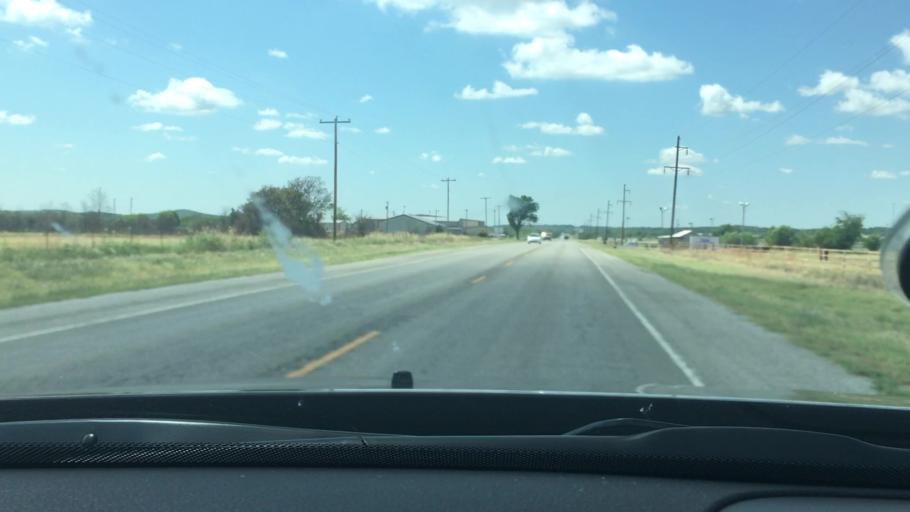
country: US
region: Oklahoma
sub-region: Carter County
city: Ardmore
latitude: 34.0886
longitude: -97.1429
